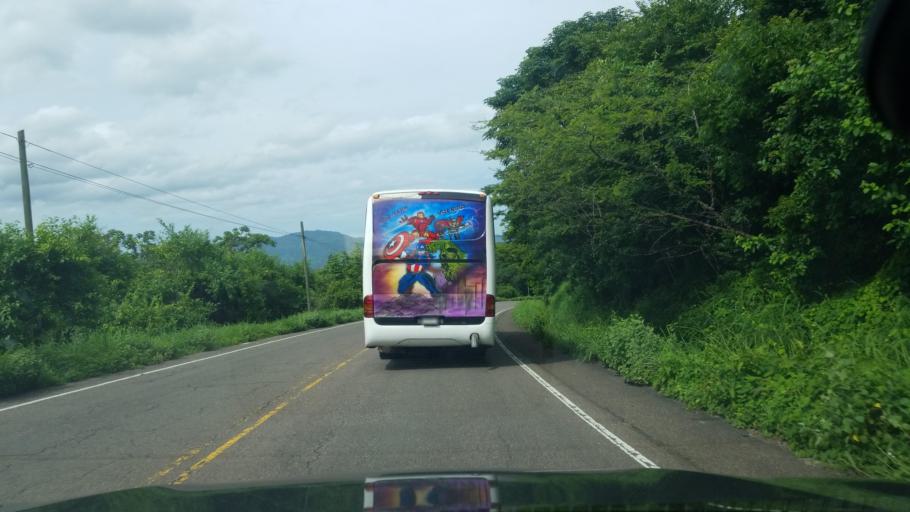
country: HN
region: Choluteca
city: Santa Ana de Yusguare
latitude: 13.3696
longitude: -87.0767
